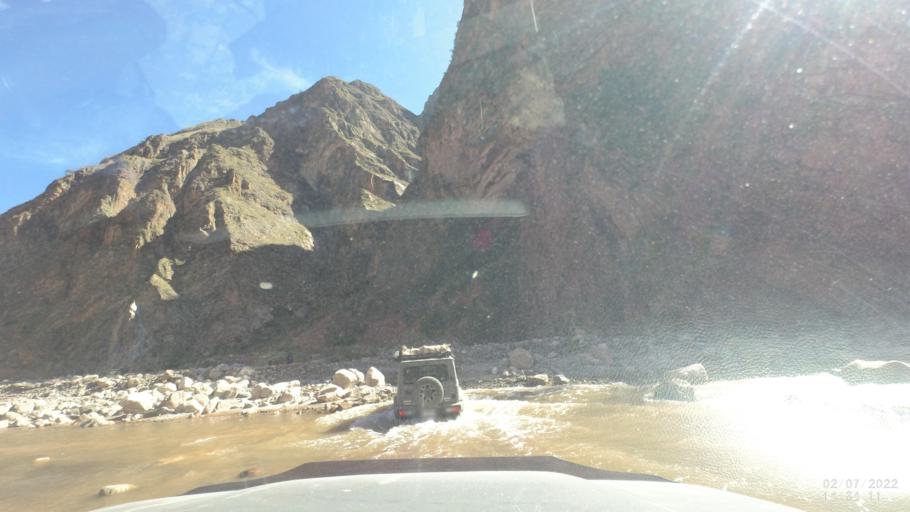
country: BO
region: Cochabamba
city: Irpa Irpa
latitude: -17.8388
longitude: -66.4167
